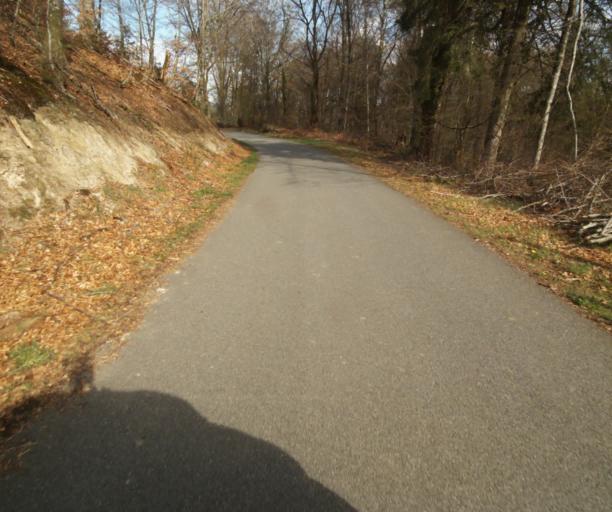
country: FR
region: Limousin
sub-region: Departement de la Correze
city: Correze
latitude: 45.3409
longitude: 1.8572
